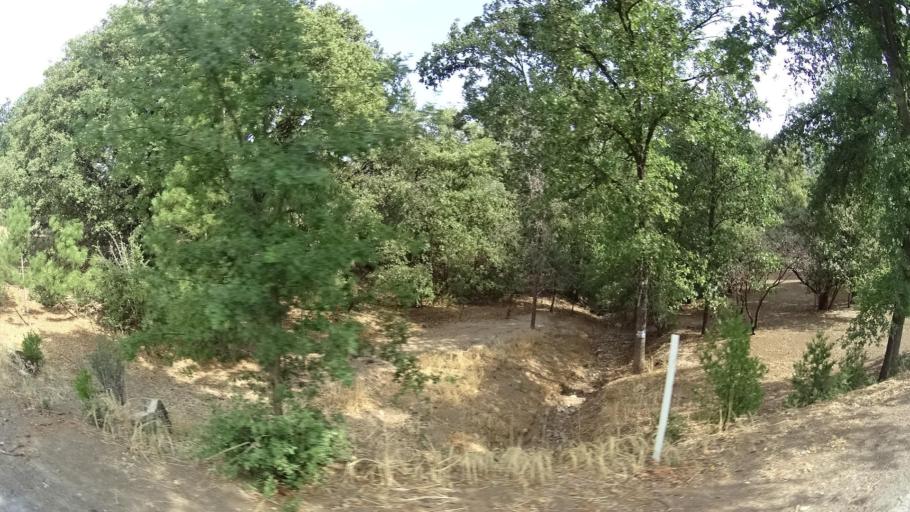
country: US
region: California
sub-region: Mariposa County
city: Midpines
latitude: 37.5012
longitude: -119.8059
